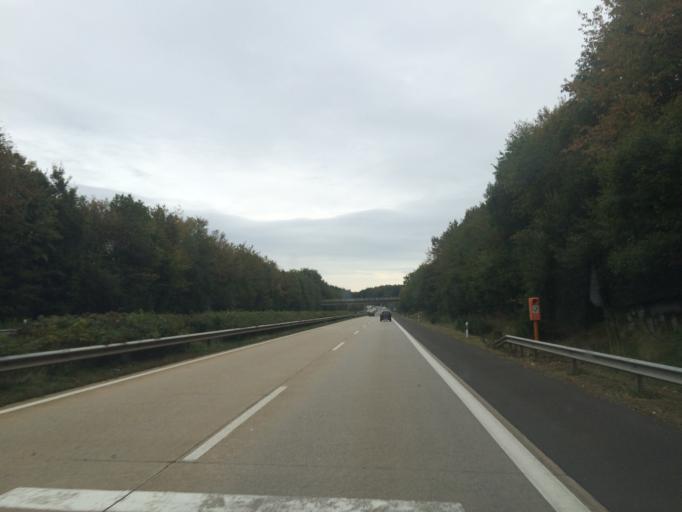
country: DE
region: Rheinland-Pfalz
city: Laufeld
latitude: 50.0849
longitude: 6.8714
